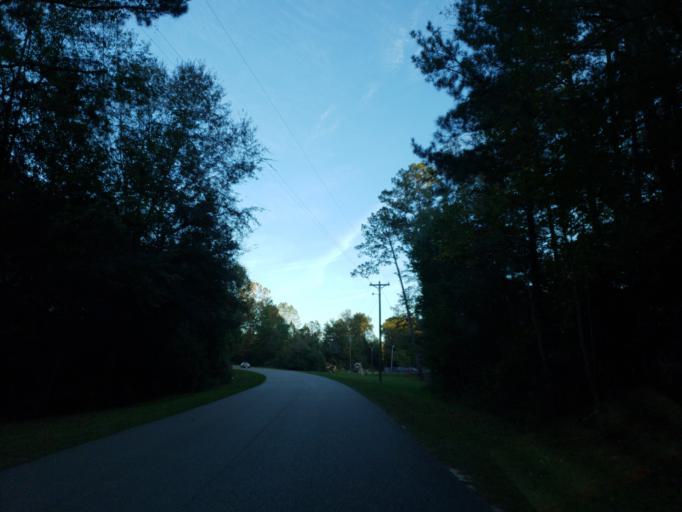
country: US
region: Mississippi
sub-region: Wayne County
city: Belmont
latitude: 31.4353
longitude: -88.4792
